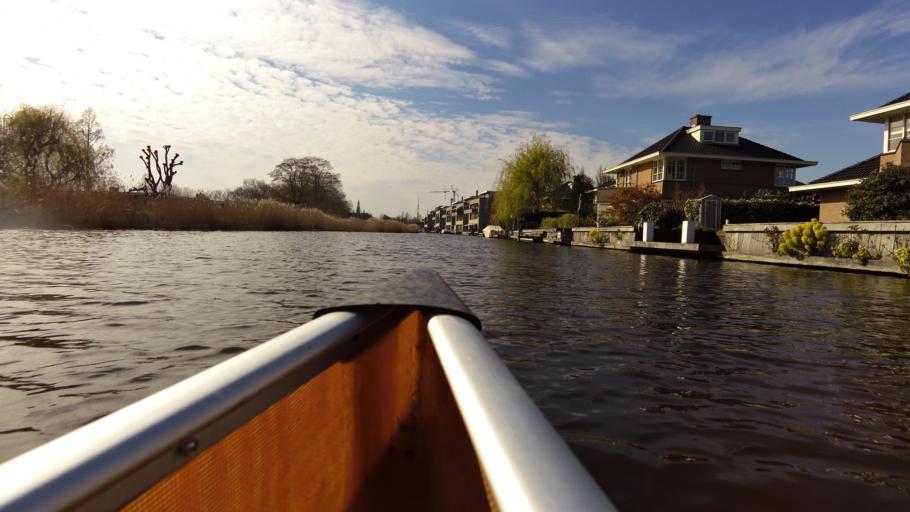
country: NL
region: South Holland
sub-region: Gemeente Lisse
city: Lisse
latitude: 52.2526
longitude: 4.5638
